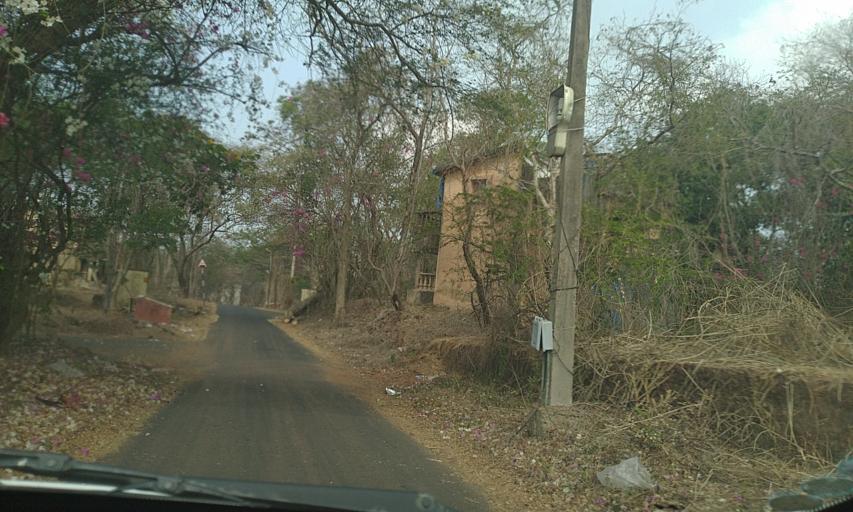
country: IN
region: Goa
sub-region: North Goa
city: Taleigao
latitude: 15.4551
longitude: 73.8371
